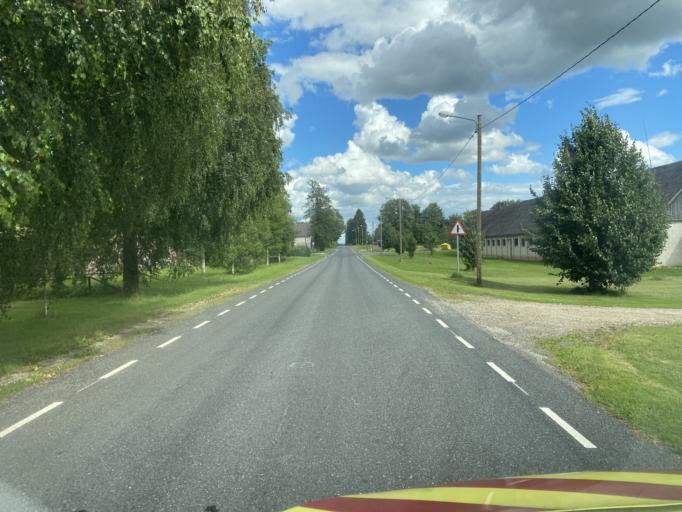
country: EE
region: Viljandimaa
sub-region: Viiratsi vald
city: Viiratsi
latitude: 58.3898
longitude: 25.7419
